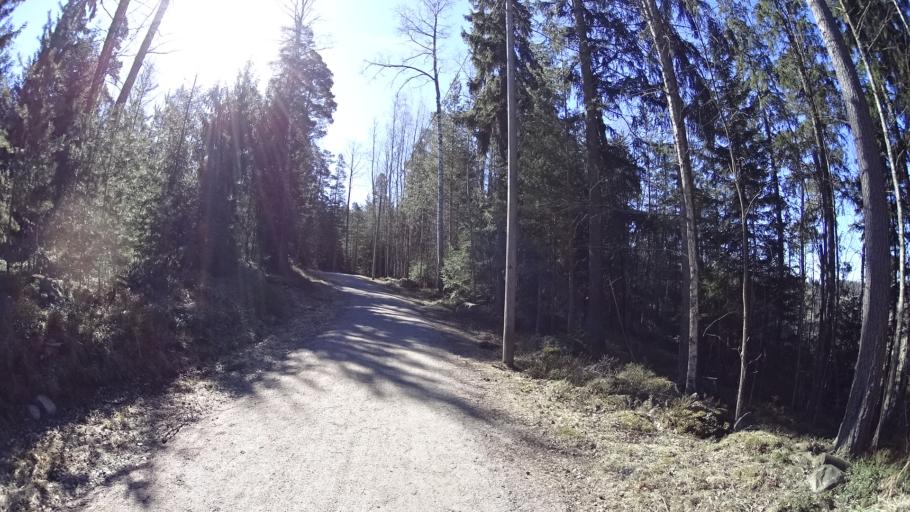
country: FI
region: Uusimaa
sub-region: Helsinki
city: Kilo
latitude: 60.2293
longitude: 24.7970
